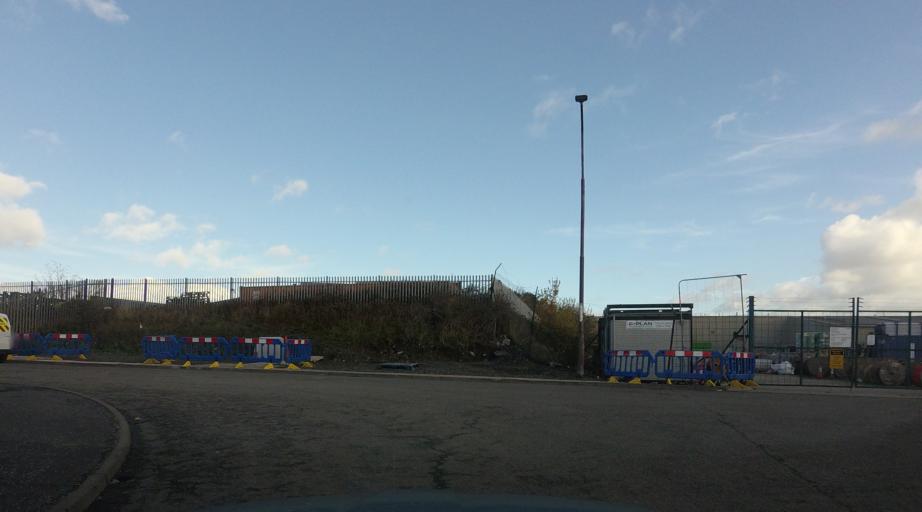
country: GB
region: Scotland
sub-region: West Lothian
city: Broxburn
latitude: 55.9423
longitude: -3.4543
